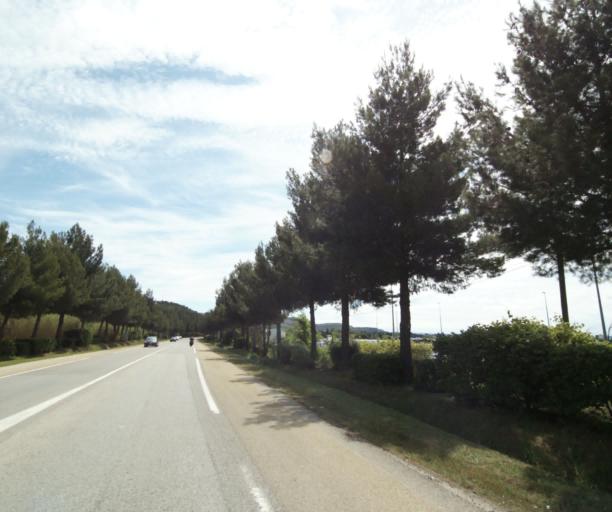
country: FR
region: Provence-Alpes-Cote d'Azur
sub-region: Departement des Bouches-du-Rhone
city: Rognac
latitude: 43.4998
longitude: 5.2270
